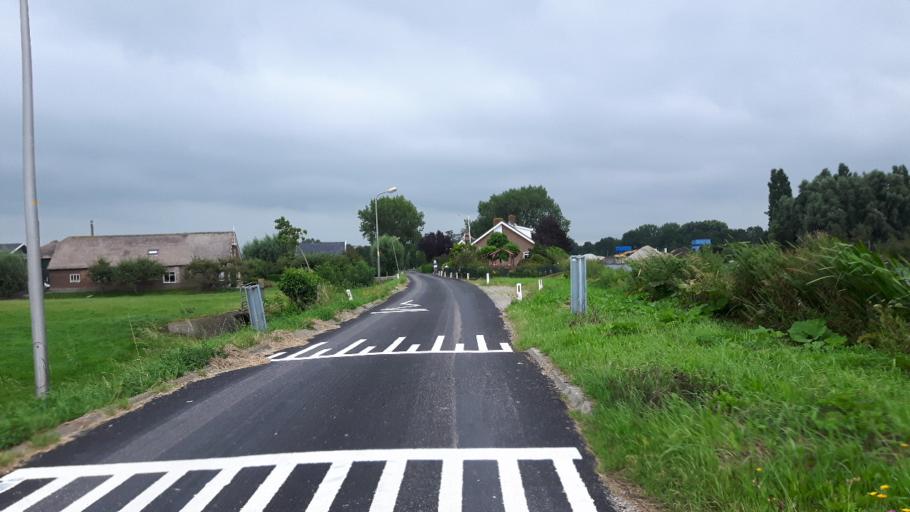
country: NL
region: South Holland
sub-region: Bodegraven-Reeuwijk
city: Bodegraven
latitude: 52.1129
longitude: 4.7095
